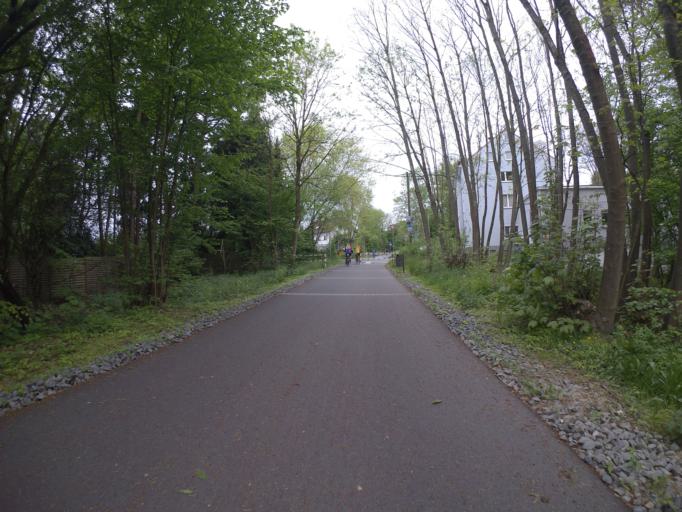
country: DE
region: North Rhine-Westphalia
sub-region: Regierungsbezirk Arnsberg
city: Schwelm
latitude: 51.2939
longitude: 7.2430
